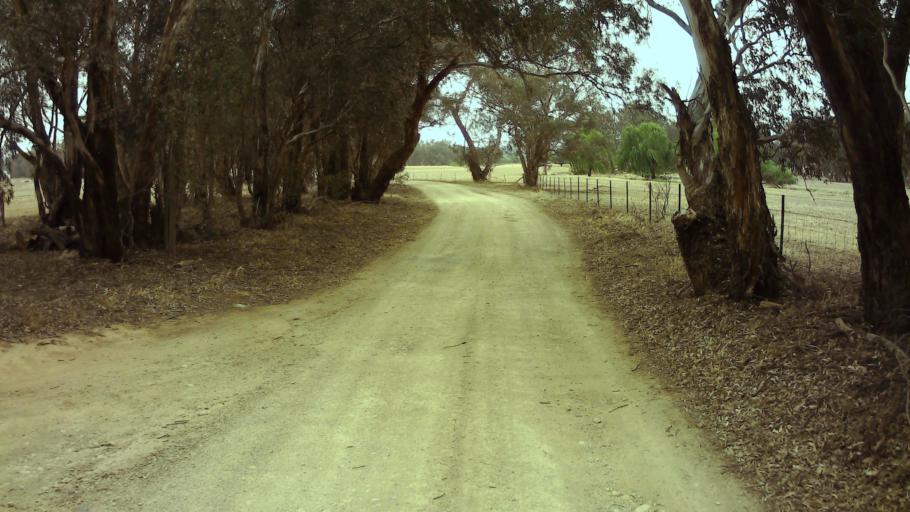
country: AU
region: New South Wales
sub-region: Weddin
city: Grenfell
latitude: -33.9028
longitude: 148.1414
